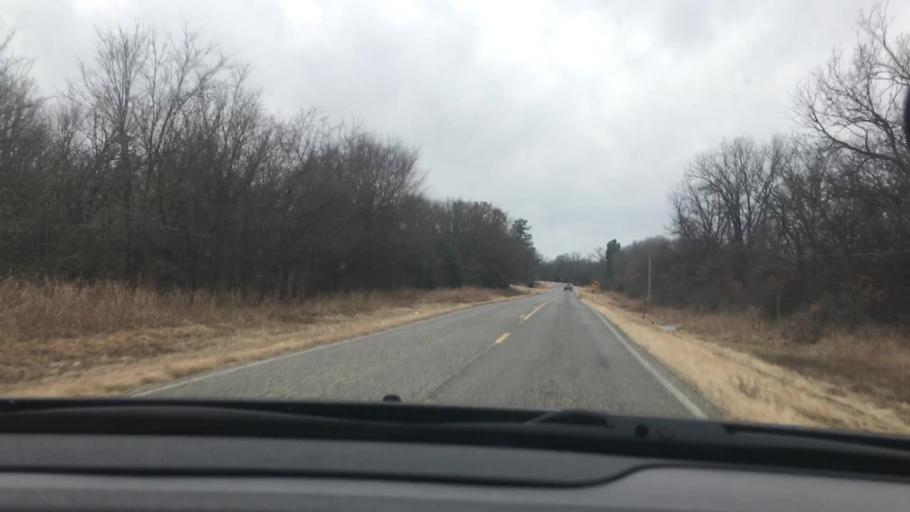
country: US
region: Oklahoma
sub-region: Johnston County
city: Tishomingo
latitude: 34.2136
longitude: -96.6362
